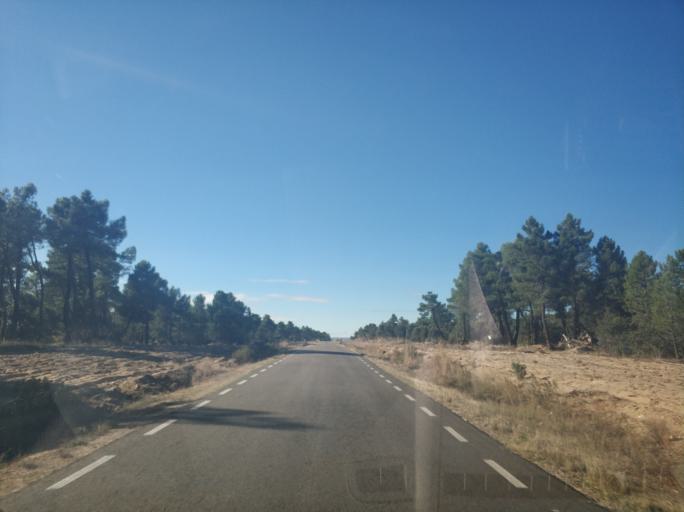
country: ES
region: Castille and Leon
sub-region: Provincia de Burgos
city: San Juan del Monte
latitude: 41.6665
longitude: -3.5291
